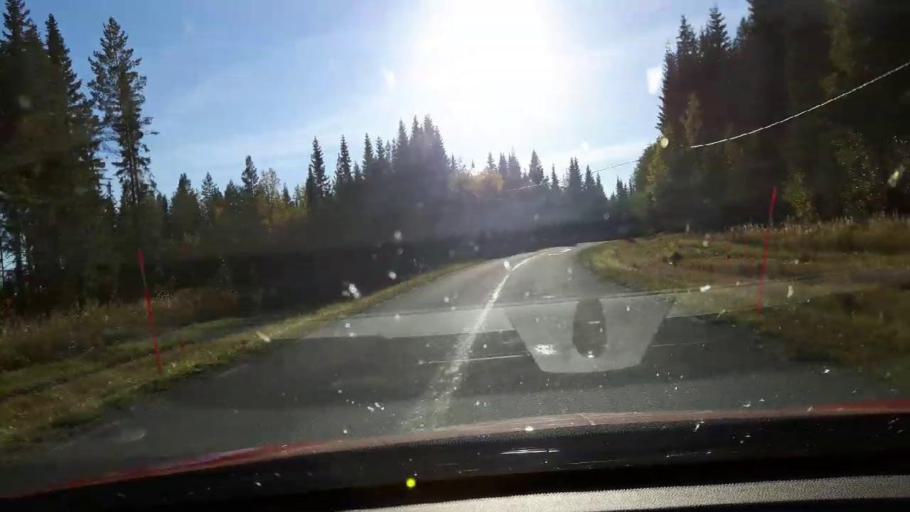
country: SE
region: Jaemtland
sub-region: OEstersunds Kommun
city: Lit
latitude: 63.8224
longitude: 14.8492
